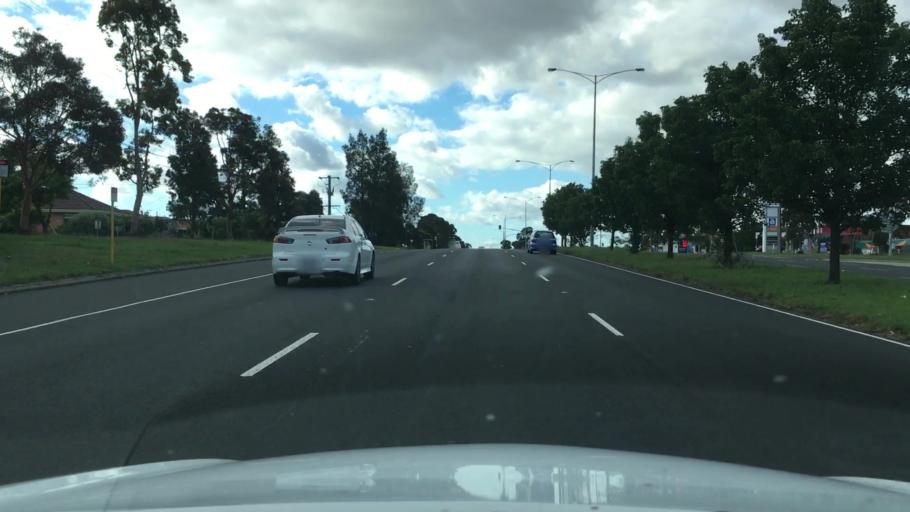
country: AU
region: Victoria
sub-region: Greater Dandenong
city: Springvale
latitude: -37.9431
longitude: 145.1676
